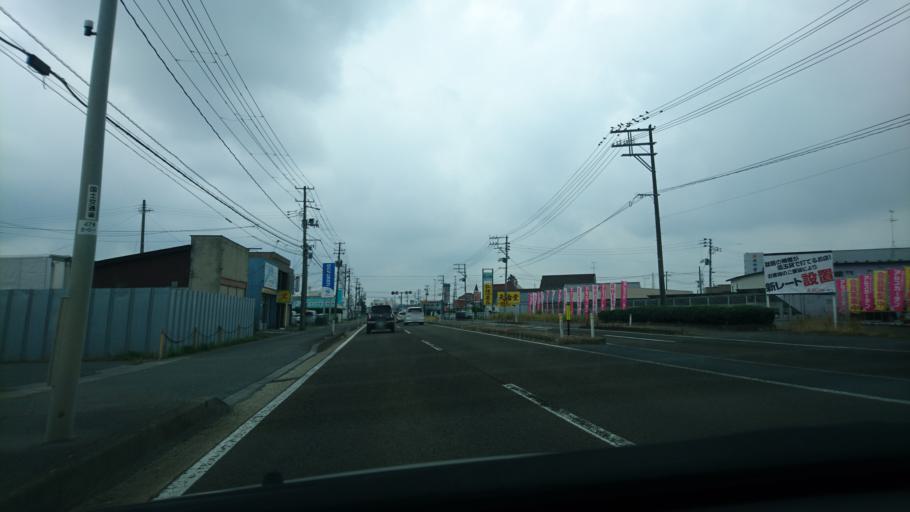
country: JP
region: Miyagi
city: Furukawa
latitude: 38.5880
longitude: 140.9416
